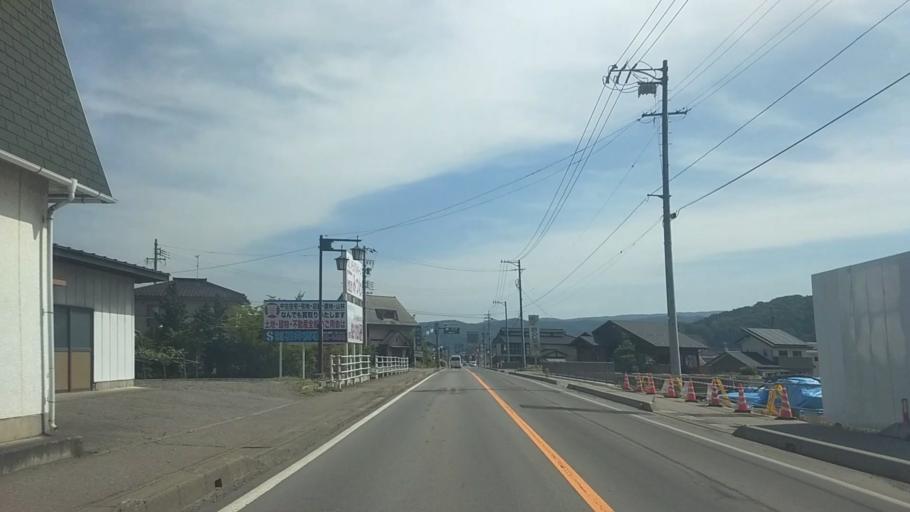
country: JP
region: Nagano
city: Saku
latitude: 36.1577
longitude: 138.4796
